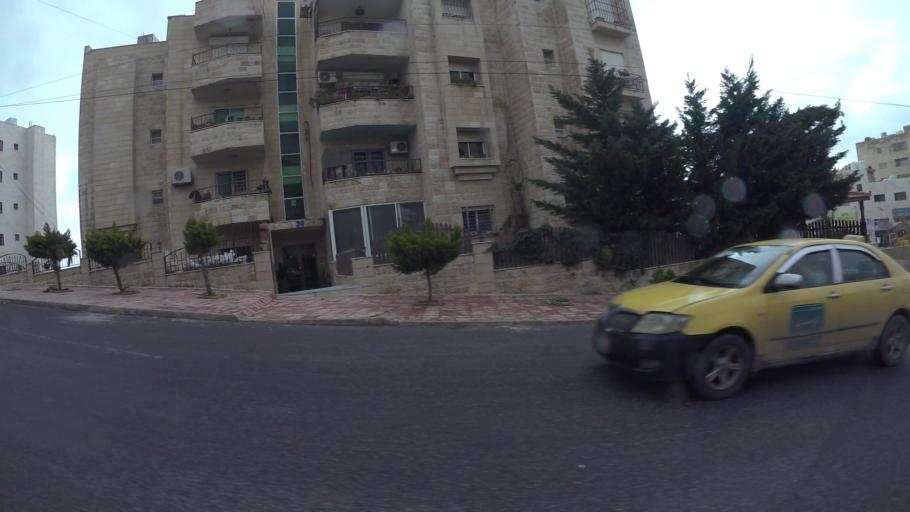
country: JO
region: Amman
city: Al Jubayhah
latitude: 31.9909
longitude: 35.8585
